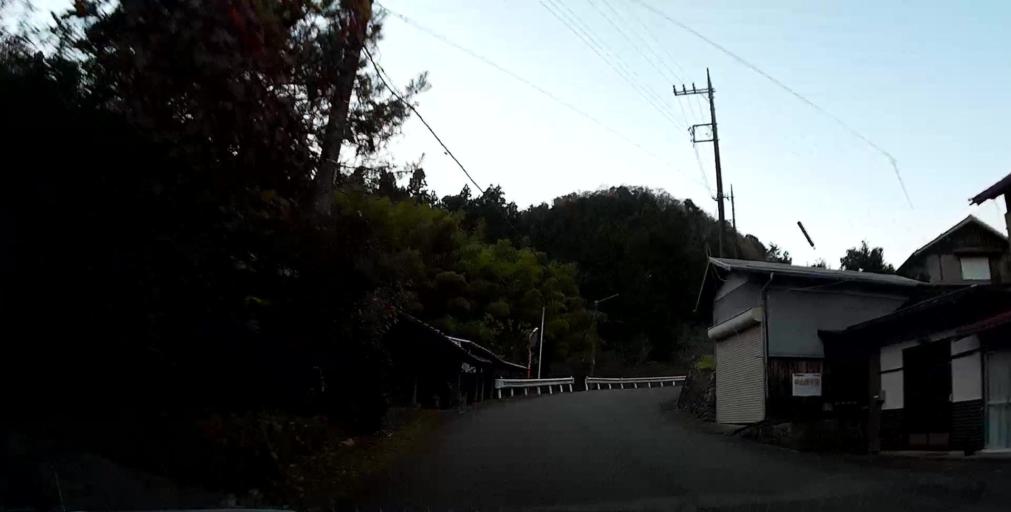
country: JP
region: Yamanashi
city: Uenohara
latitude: 35.5752
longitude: 139.1892
